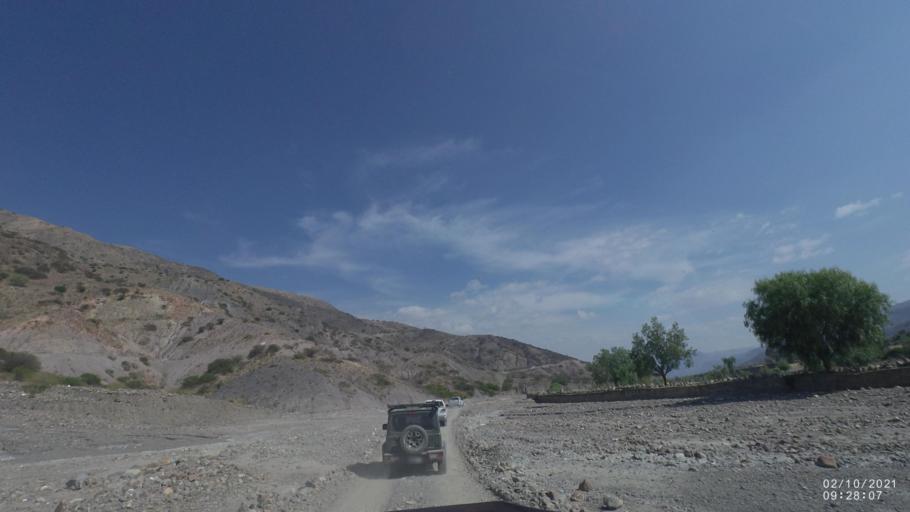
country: BO
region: Cochabamba
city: Irpa Irpa
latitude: -17.8537
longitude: -66.3175
